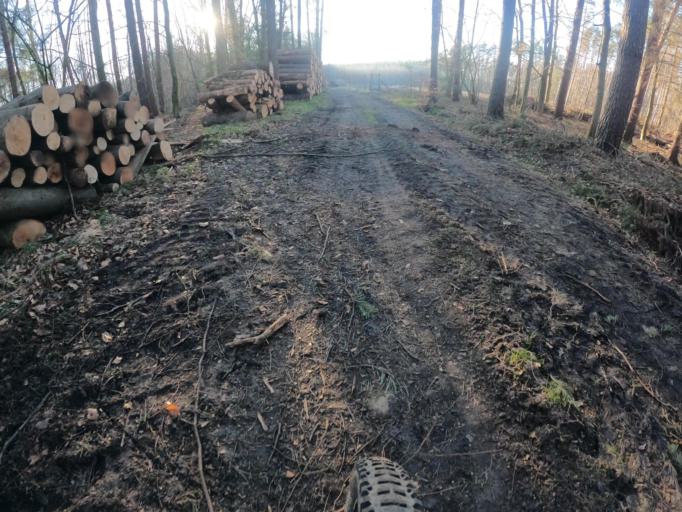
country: PL
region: West Pomeranian Voivodeship
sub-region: Powiat gryficki
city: Brojce
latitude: 53.9588
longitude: 15.3810
